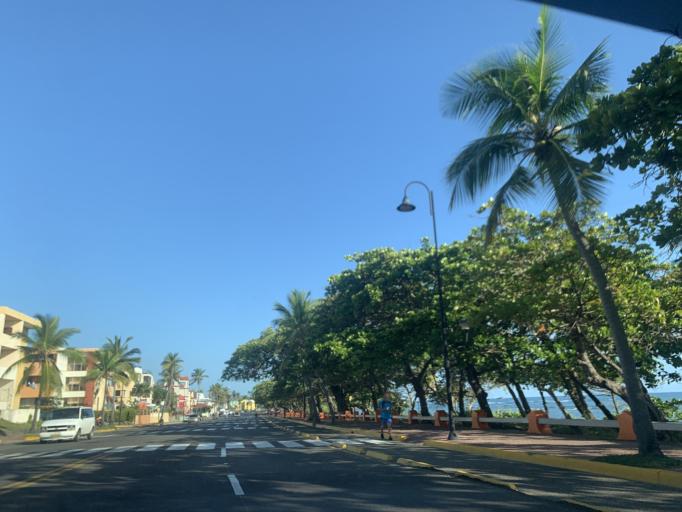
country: DO
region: Puerto Plata
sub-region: Puerto Plata
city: Puerto Plata
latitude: 19.7984
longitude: -70.6886
